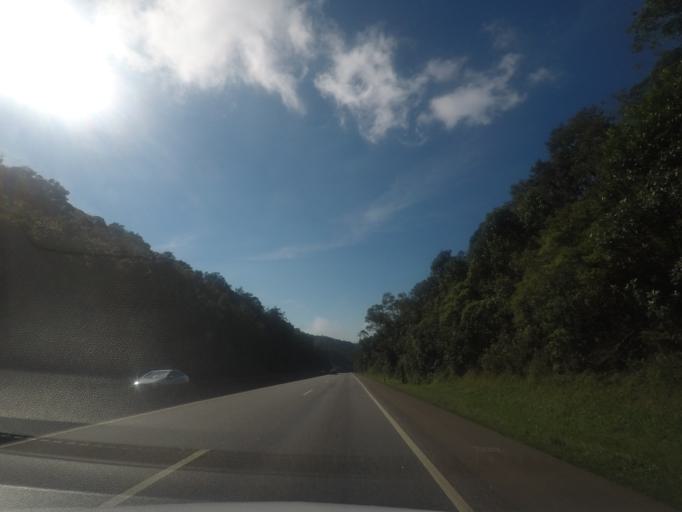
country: BR
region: Parana
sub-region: Piraquara
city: Piraquara
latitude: -25.5915
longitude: -48.9209
